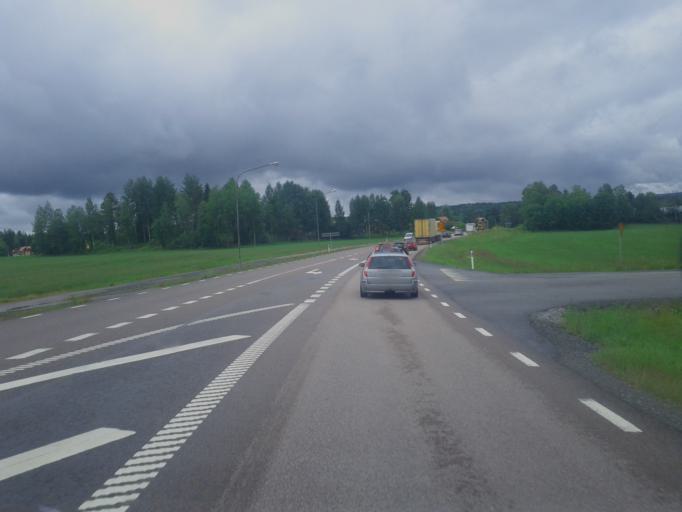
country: SE
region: Vaesternorrland
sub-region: Haernoesands Kommun
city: Haernoesand
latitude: 62.6679
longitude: 17.8420
